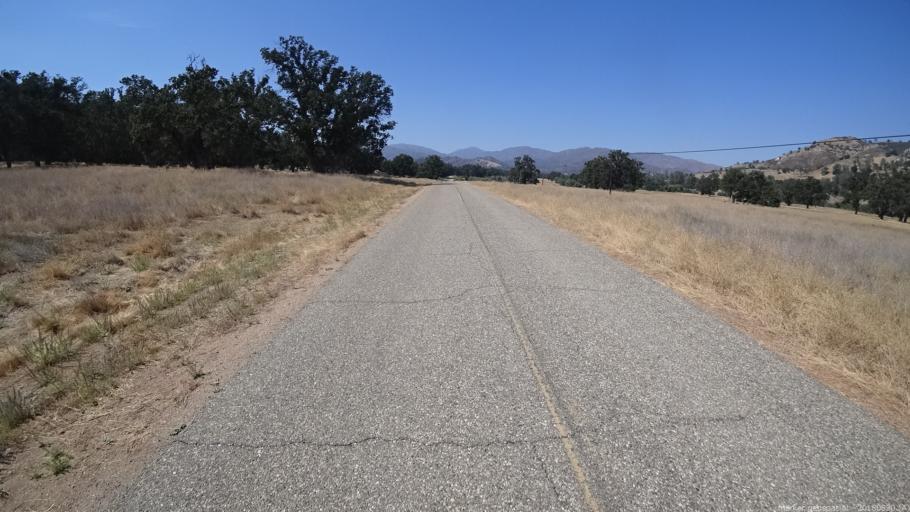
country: US
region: California
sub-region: Monterey County
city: King City
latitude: 36.0431
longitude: -121.2976
